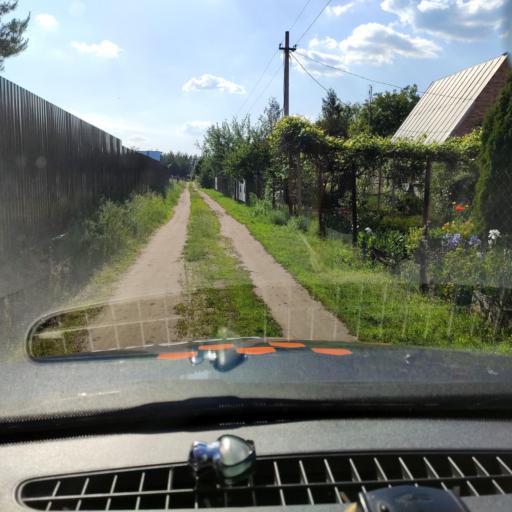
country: RU
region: Voronezj
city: Ramon'
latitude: 51.8940
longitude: 39.2031
